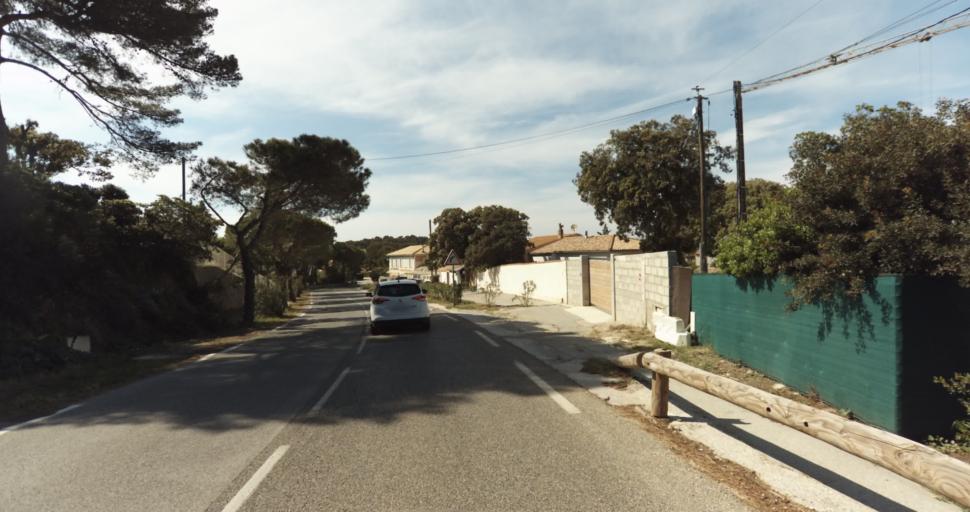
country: FR
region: Provence-Alpes-Cote d'Azur
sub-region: Departement du Var
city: Hyeres
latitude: 43.0344
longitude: 6.1451
